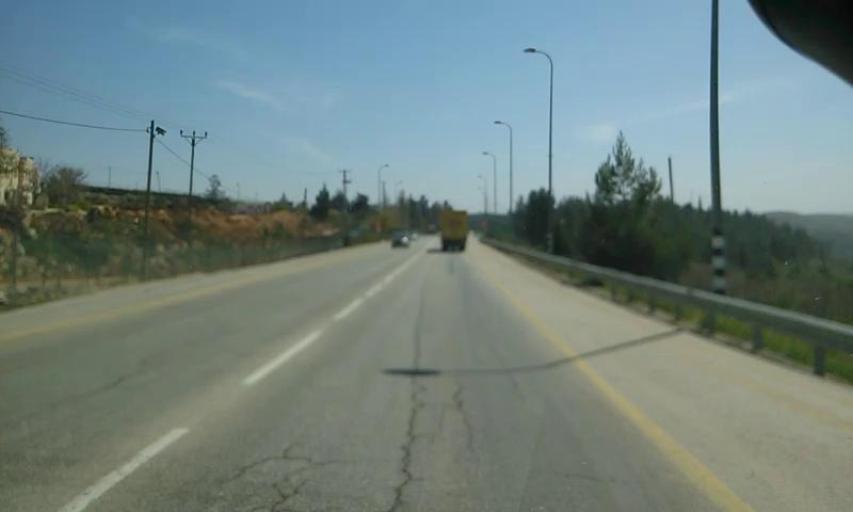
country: PS
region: West Bank
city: Bayt Ummar
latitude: 31.6498
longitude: 35.1274
